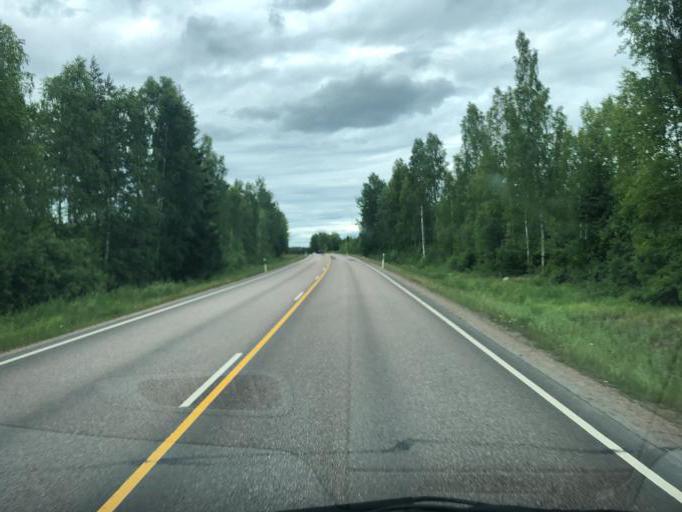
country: FI
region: Southern Savonia
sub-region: Mikkeli
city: Maentyharju
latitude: 61.1273
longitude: 27.1028
